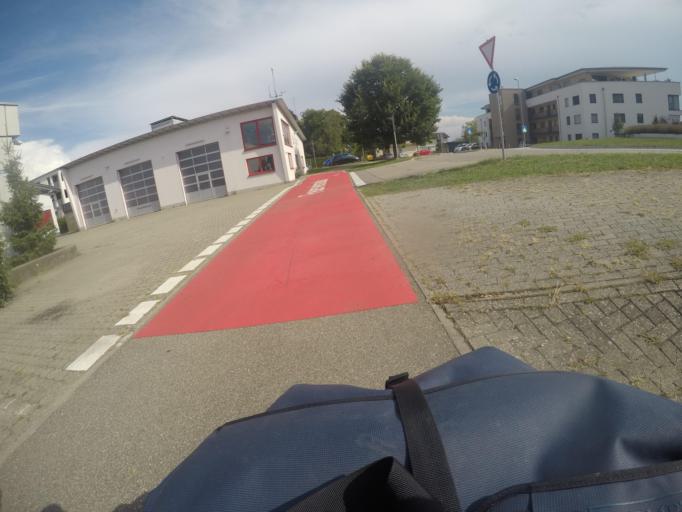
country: DE
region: Baden-Wuerttemberg
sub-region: Freiburg Region
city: Efringen-Kirchen
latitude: 47.6505
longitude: 7.5635
